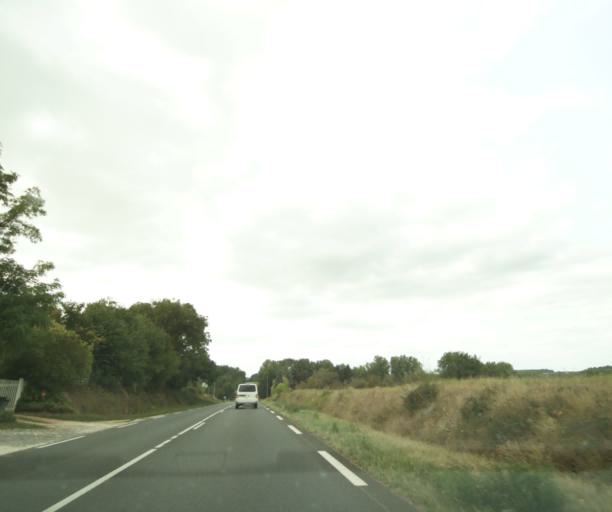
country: FR
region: Centre
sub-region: Departement d'Indre-et-Loire
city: Chambourg-sur-Indre
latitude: 47.1700
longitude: 0.9791
